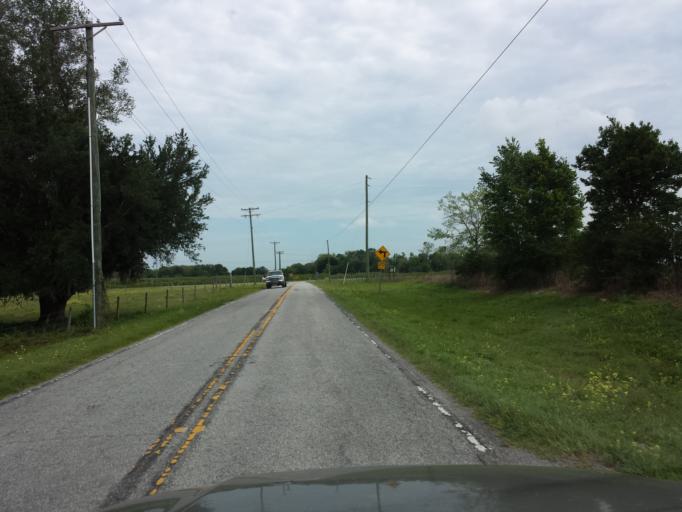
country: US
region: Florida
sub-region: Pasco County
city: San Antonio
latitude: 28.3699
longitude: -82.2746
